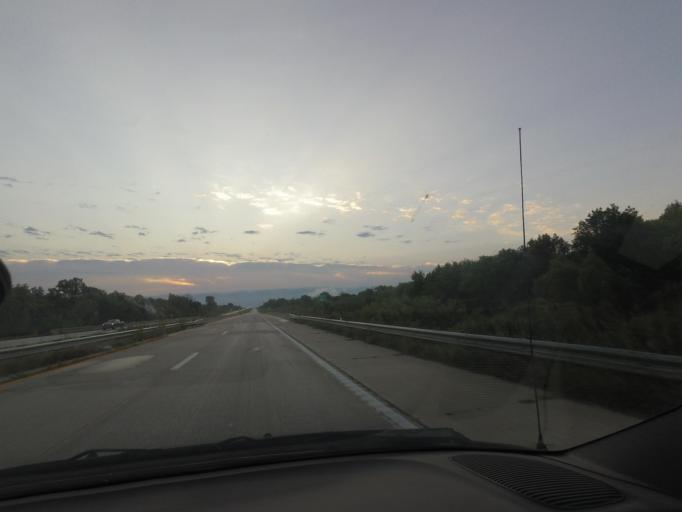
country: US
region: Missouri
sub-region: Macon County
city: Macon
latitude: 39.7524
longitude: -92.4037
